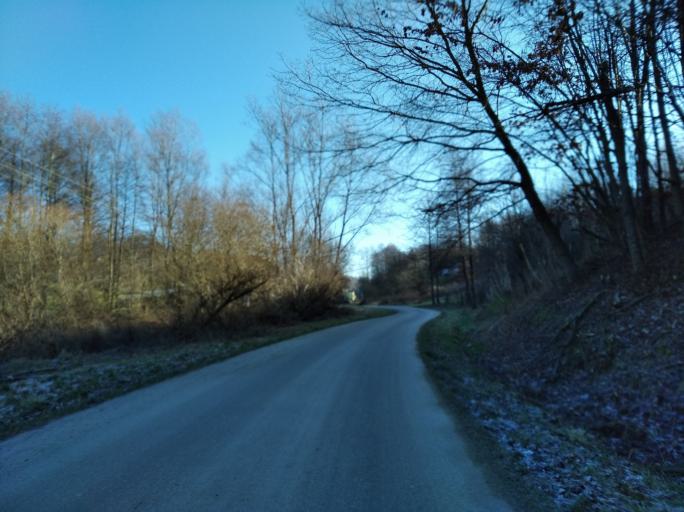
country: PL
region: Subcarpathian Voivodeship
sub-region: Powiat strzyzowski
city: Wysoka Strzyzowska
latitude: 49.8470
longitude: 21.7621
